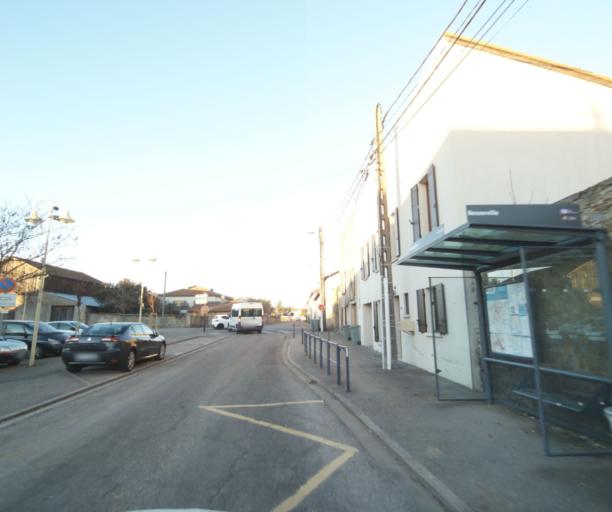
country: FR
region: Lorraine
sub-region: Departement de Meurthe-et-Moselle
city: Laneuveville-devant-Nancy
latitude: 48.6634
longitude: 6.2418
